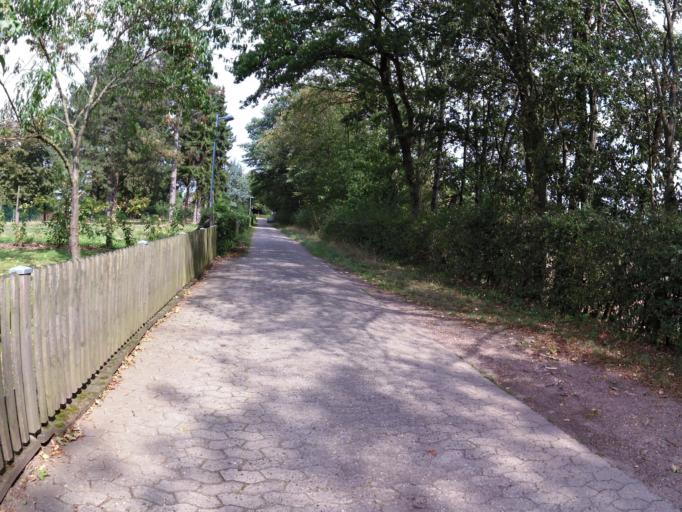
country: DE
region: Lower Saxony
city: Landesbergen
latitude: 52.5746
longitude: 9.1135
